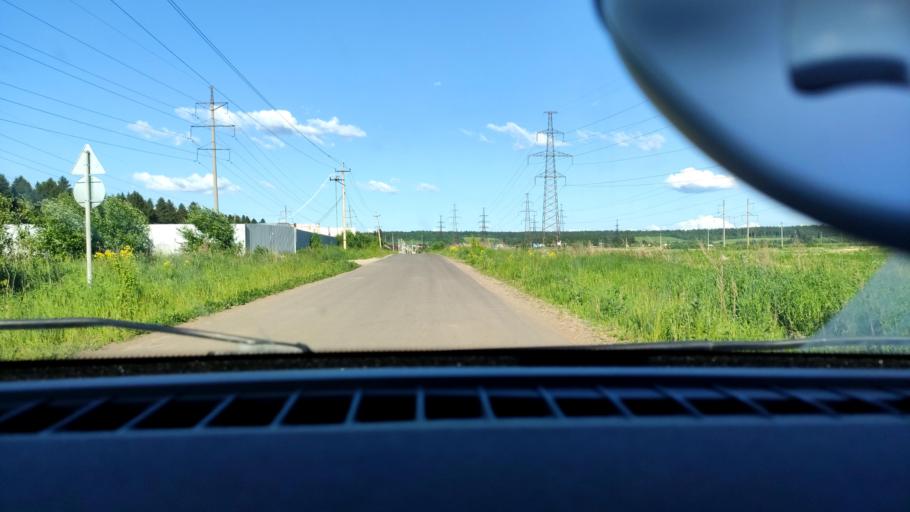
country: RU
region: Perm
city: Ferma
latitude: 57.9156
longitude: 56.3396
